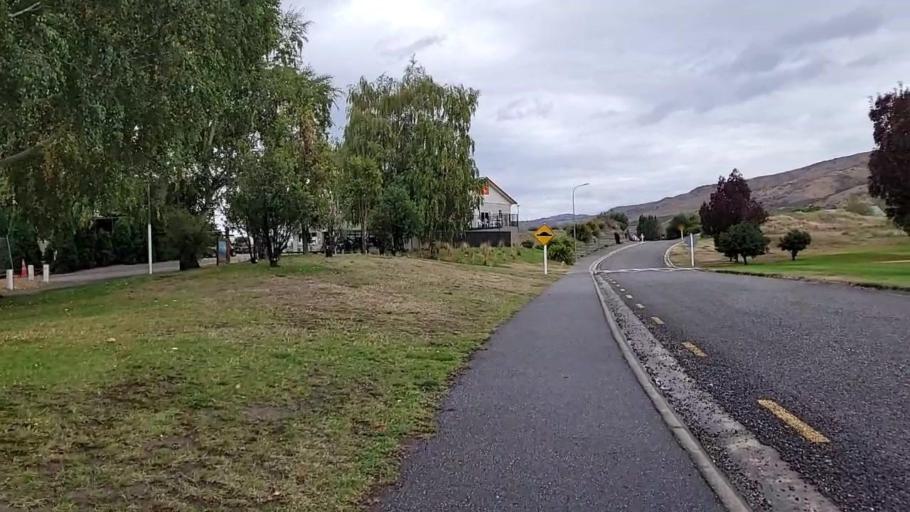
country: NZ
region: Otago
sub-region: Queenstown-Lakes District
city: Wanaka
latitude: -45.0402
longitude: 169.2081
